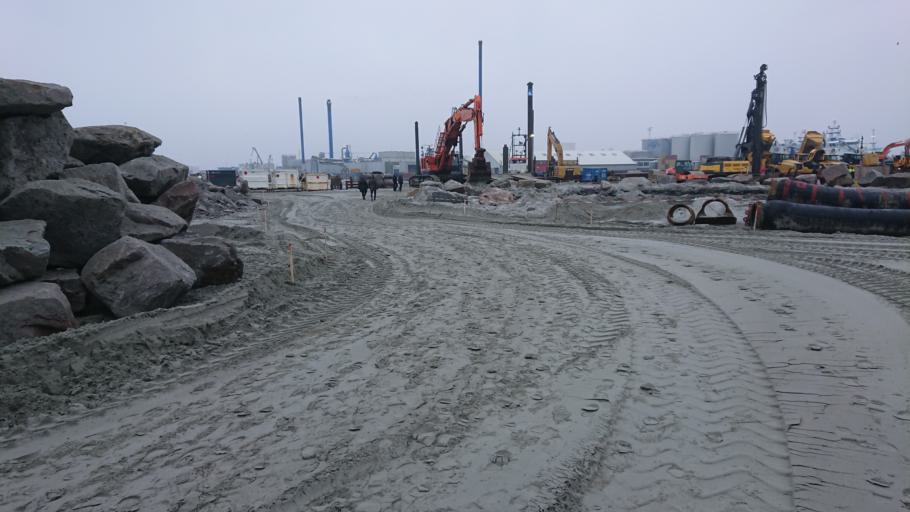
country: DK
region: North Denmark
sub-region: Frederikshavn Kommune
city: Skagen
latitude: 57.7198
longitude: 10.6065
